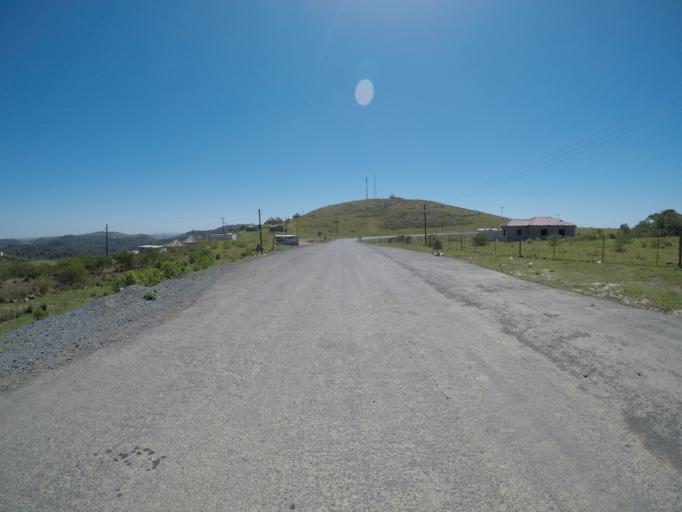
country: ZA
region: Eastern Cape
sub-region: OR Tambo District Municipality
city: Libode
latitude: -32.0016
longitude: 29.1167
